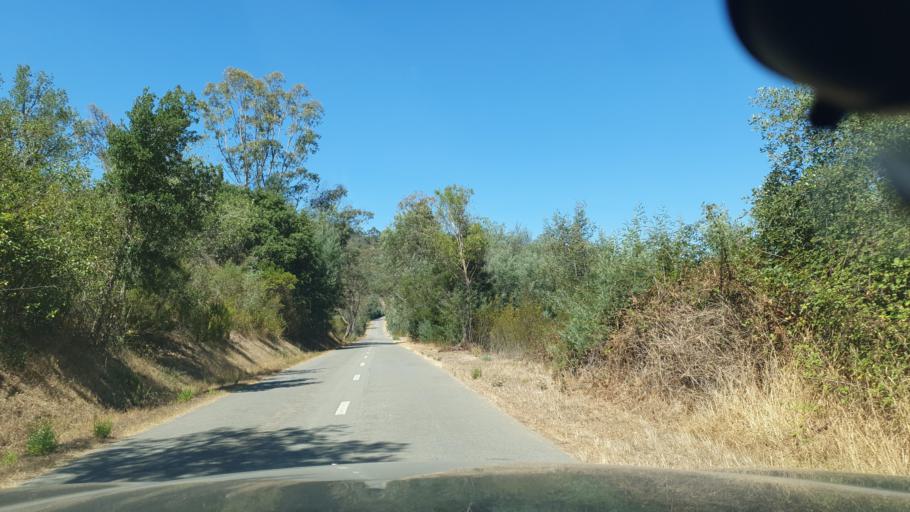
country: PT
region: Beja
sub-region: Odemira
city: Odemira
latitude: 37.5072
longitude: -8.4536
